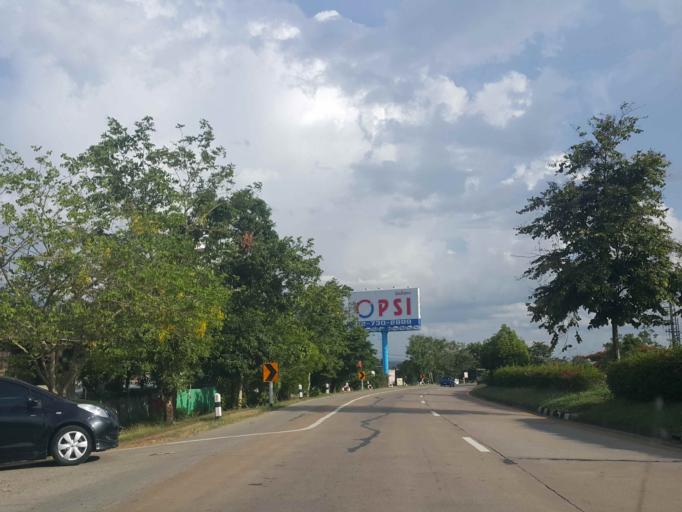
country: TH
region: Phrae
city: Sung Men
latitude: 18.0260
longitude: 100.1111
